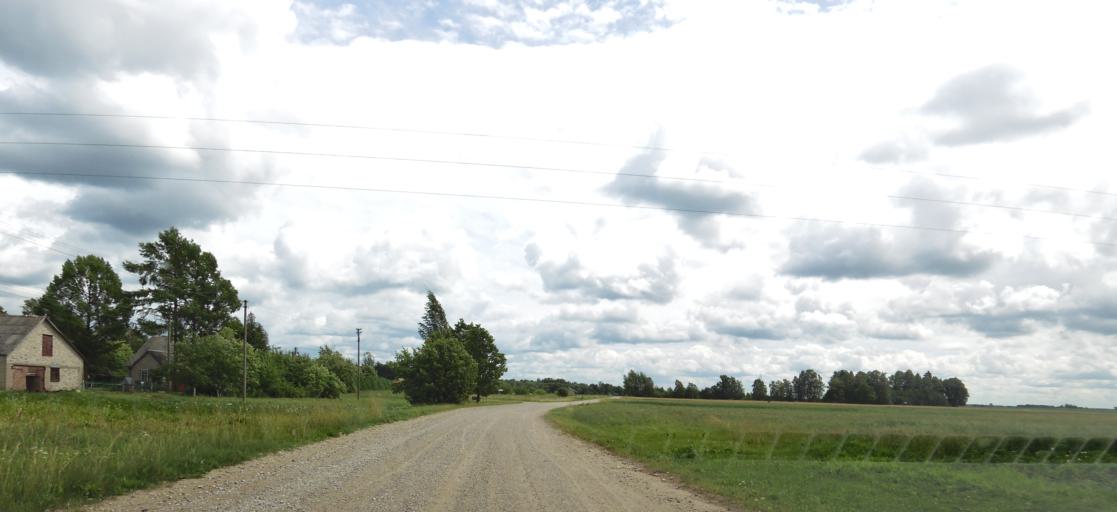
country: LT
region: Panevezys
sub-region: Birzai
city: Birzai
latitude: 56.3171
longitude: 24.7961
